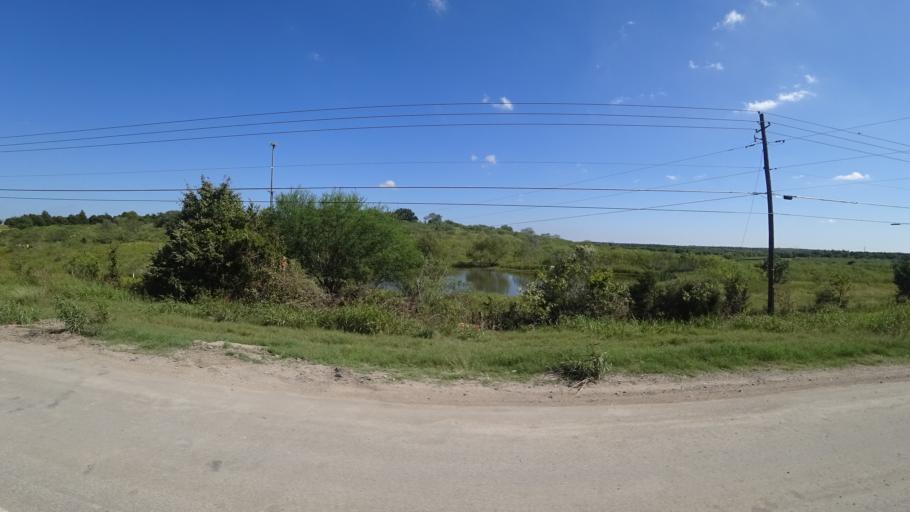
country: US
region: Texas
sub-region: Travis County
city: Manor
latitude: 30.3327
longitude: -97.6019
